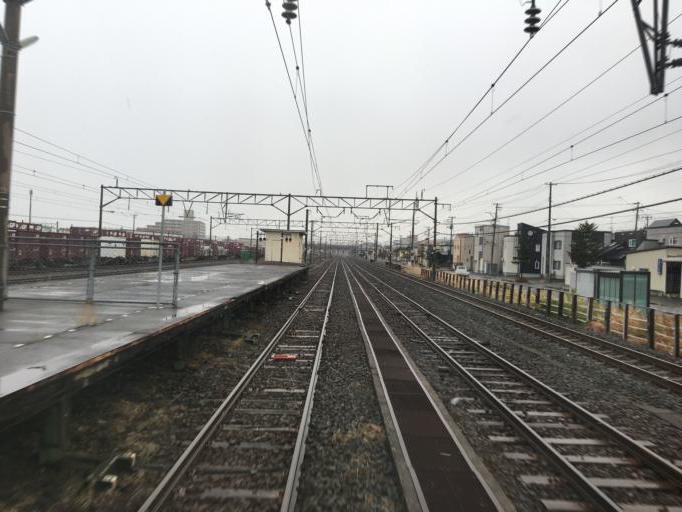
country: JP
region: Aomori
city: Aomori Shi
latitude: 40.8110
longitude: 140.7842
